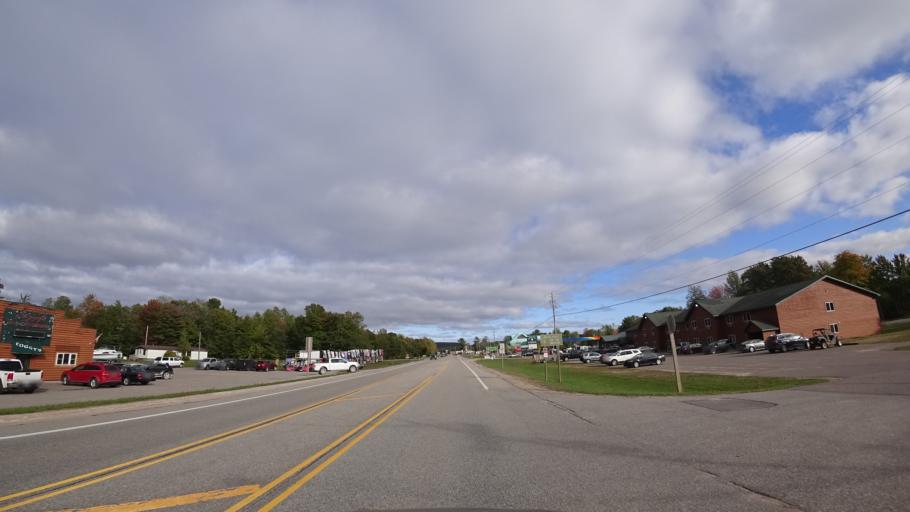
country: US
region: Michigan
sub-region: Alger County
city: Munising
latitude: 46.4385
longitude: -86.7104
